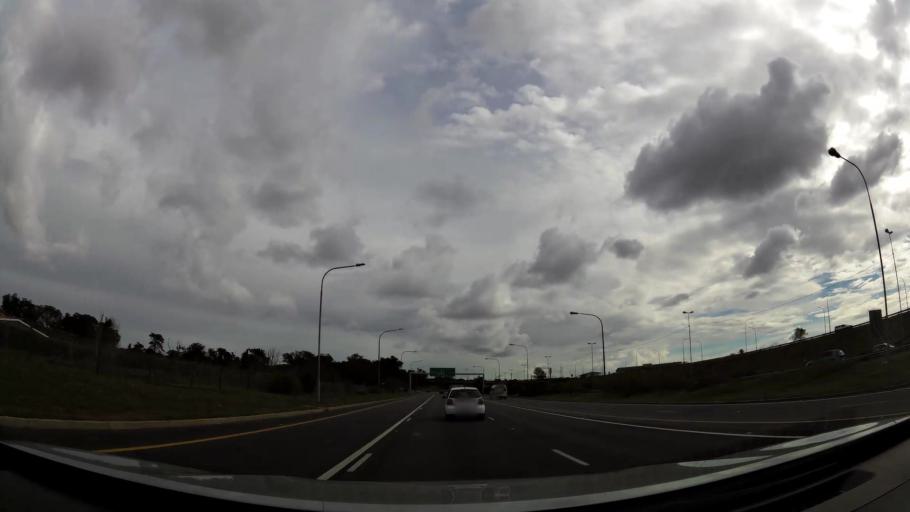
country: ZA
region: Eastern Cape
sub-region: Nelson Mandela Bay Metropolitan Municipality
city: Port Elizabeth
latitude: -33.9458
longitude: 25.5359
